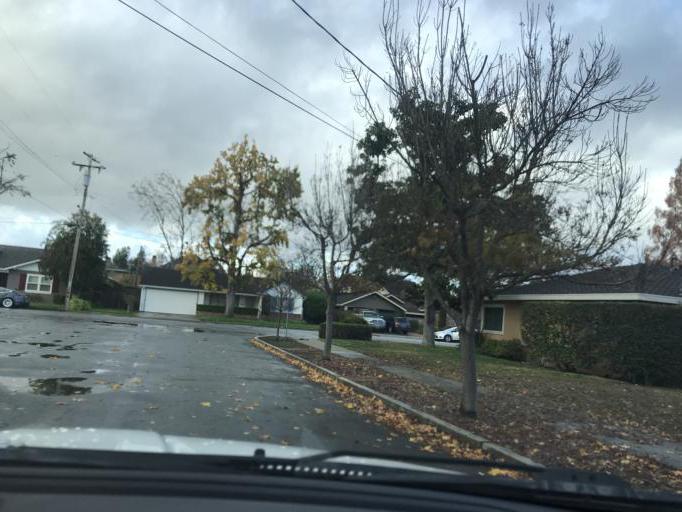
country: US
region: California
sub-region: Santa Clara County
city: Buena Vista
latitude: 37.2990
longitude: -121.9172
